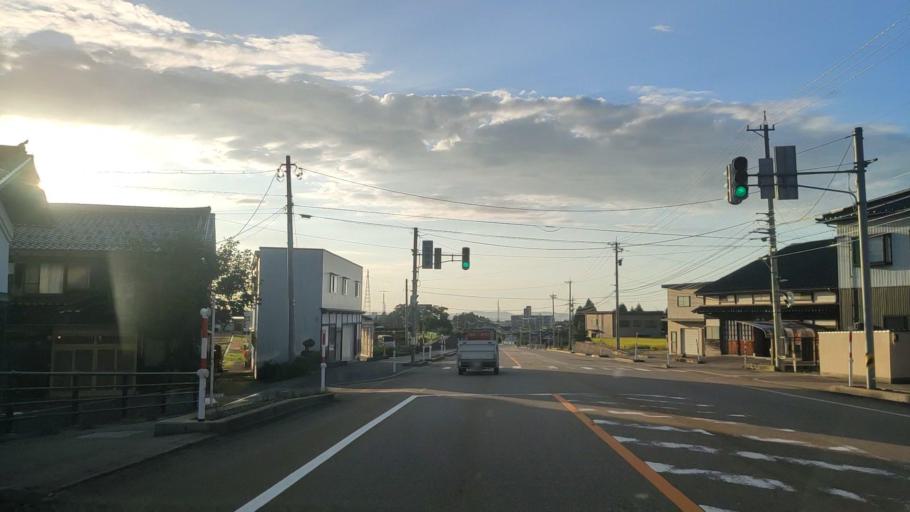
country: JP
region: Toyama
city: Nanto-shi
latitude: 36.5707
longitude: 136.9890
